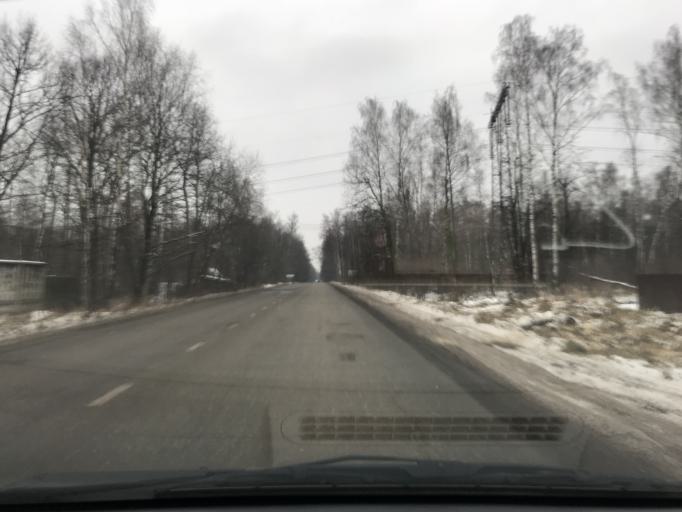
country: RU
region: Moskovskaya
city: Elektrostal'
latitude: 55.8200
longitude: 38.4550
